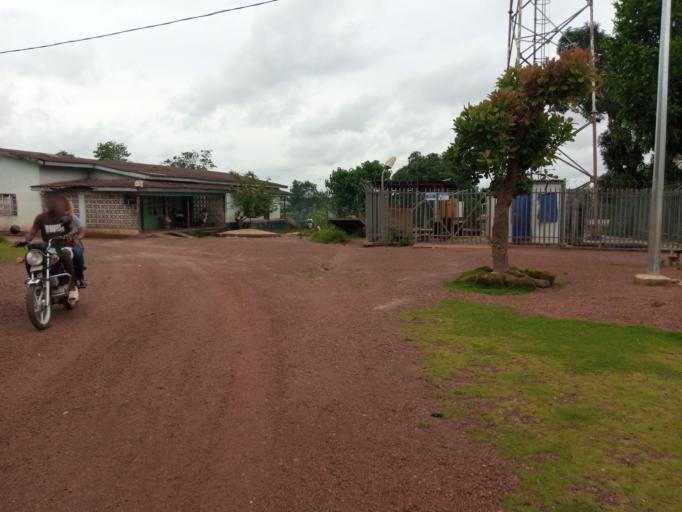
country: SL
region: Southern Province
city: Largo
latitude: 8.2006
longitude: -12.0589
